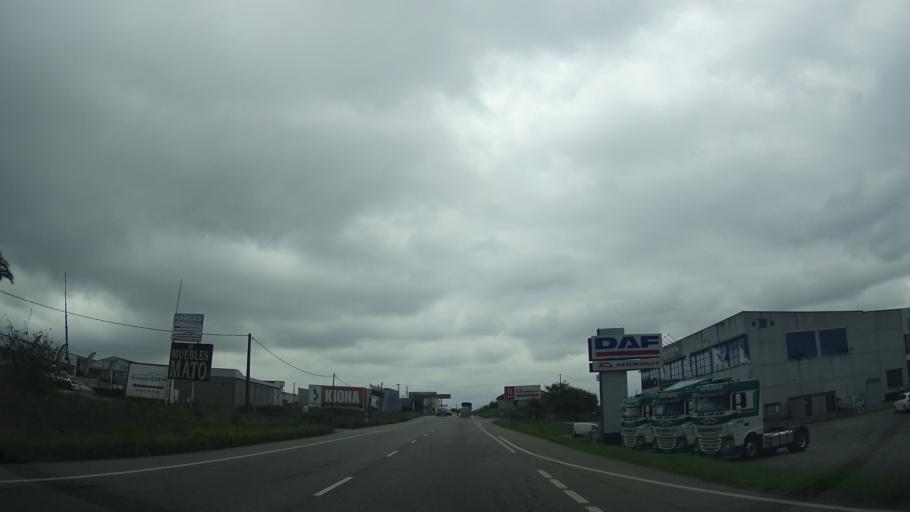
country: ES
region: Asturias
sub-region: Province of Asturias
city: Norena
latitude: 43.3833
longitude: -5.7536
